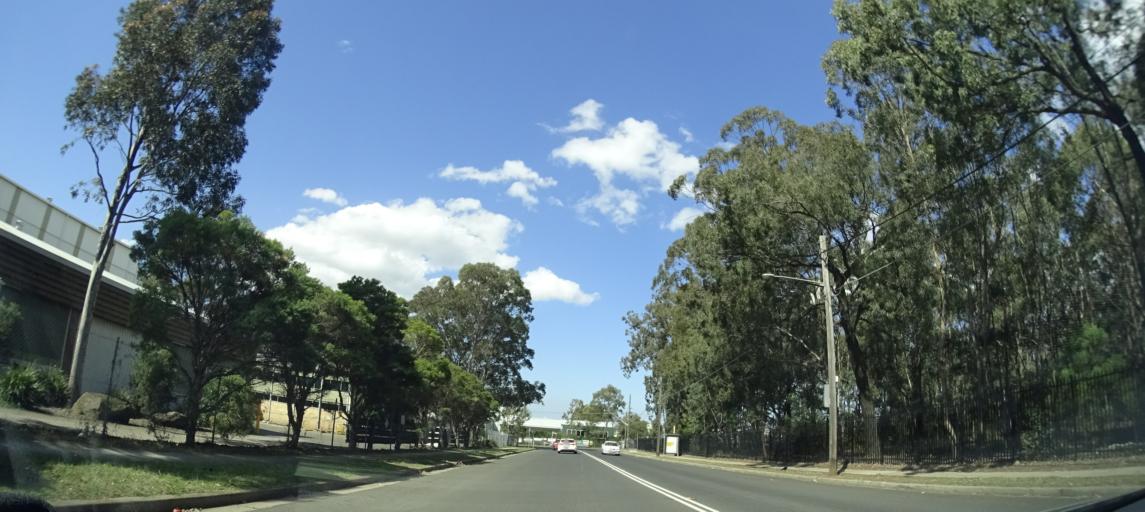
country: AU
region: New South Wales
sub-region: Bankstown
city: Milperra
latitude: -33.9384
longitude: 150.9934
